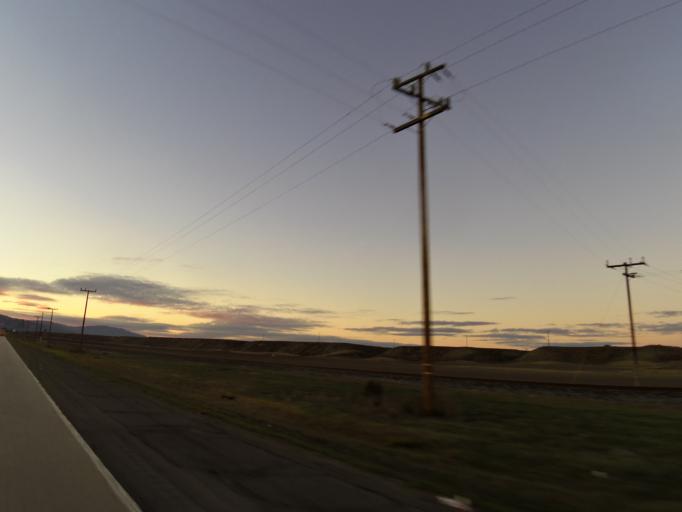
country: US
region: California
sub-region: Monterey County
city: King City
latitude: 36.1928
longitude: -121.0849
